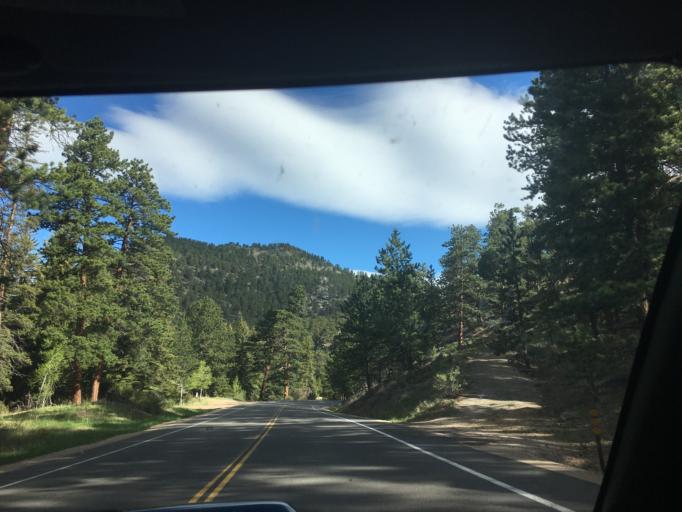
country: US
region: Colorado
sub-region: Larimer County
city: Estes Park
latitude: 40.3464
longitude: -105.5682
